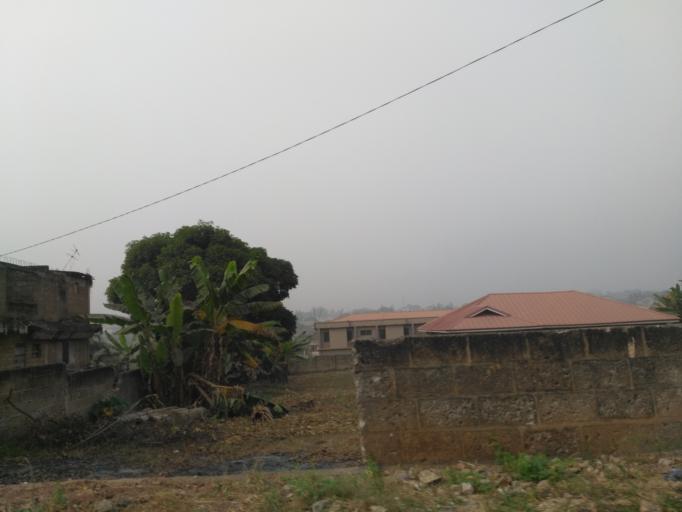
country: GH
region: Ashanti
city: Kumasi
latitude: 6.6545
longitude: -1.6218
